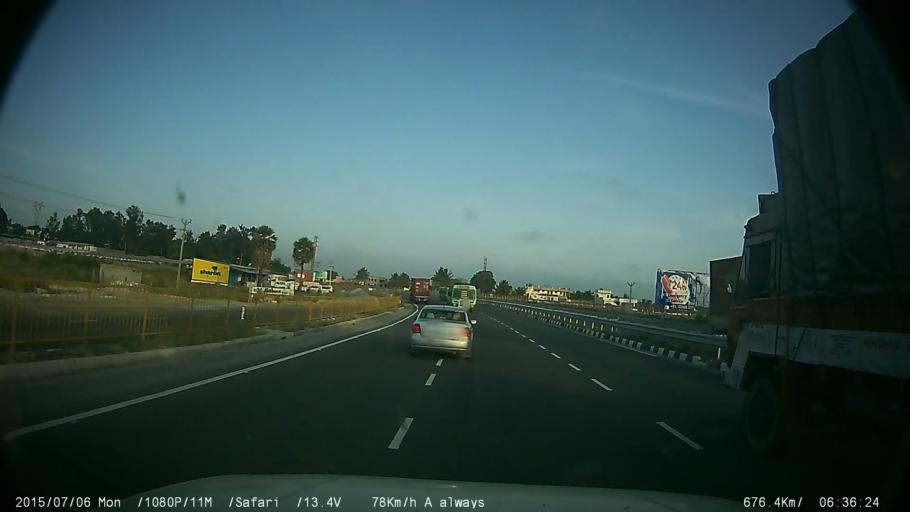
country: IN
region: Tamil Nadu
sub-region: Krishnagiri
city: Hosur
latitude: 12.7115
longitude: 77.8947
